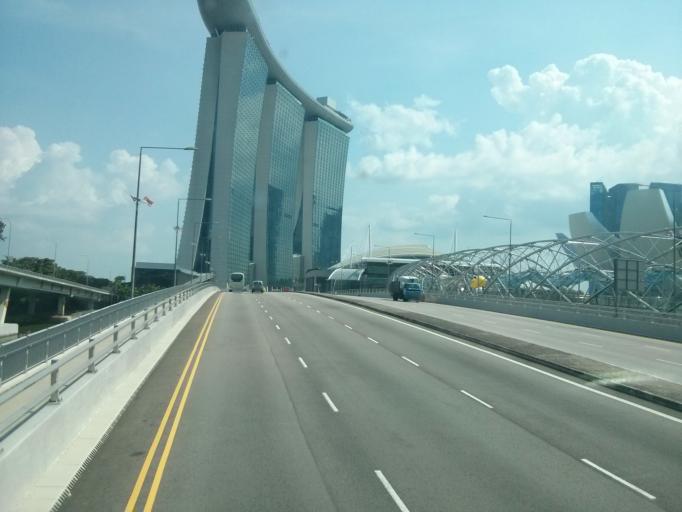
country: SG
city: Singapore
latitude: 1.2884
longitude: 103.8610
